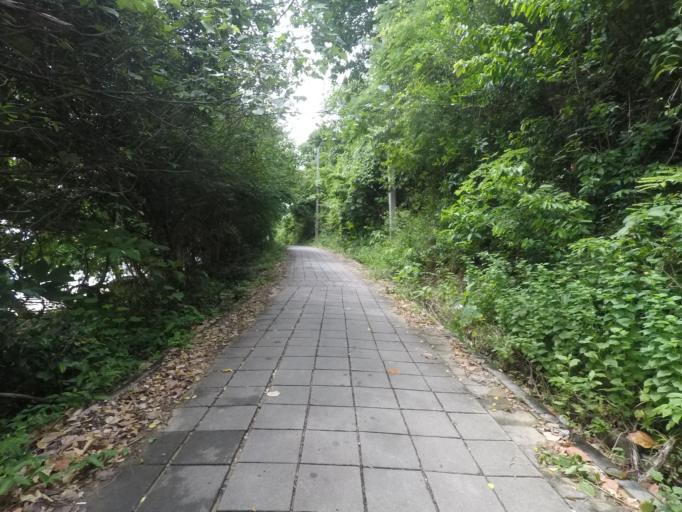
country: TH
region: Phangnga
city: Ban Phru Nai
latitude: 7.7706
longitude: 98.7675
